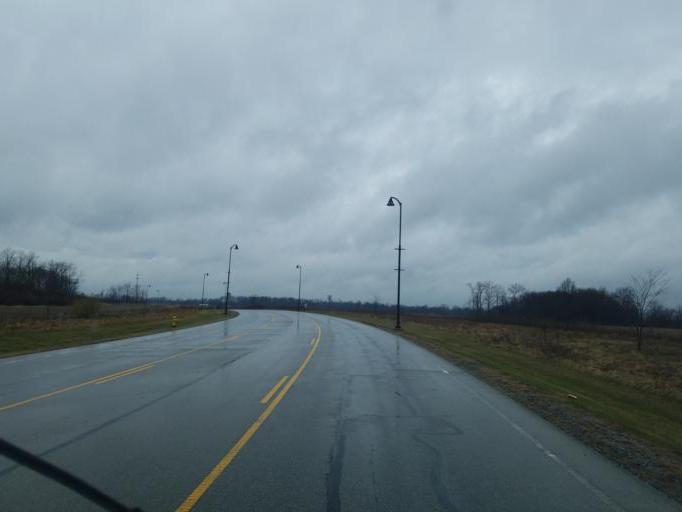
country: US
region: Ohio
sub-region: Delaware County
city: Sunbury
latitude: 40.2762
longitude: -82.9114
